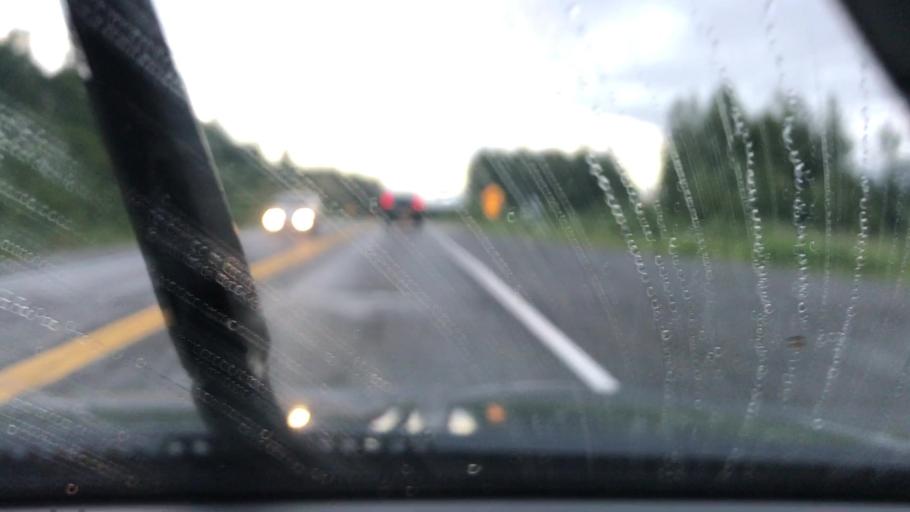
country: US
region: Alaska
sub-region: Matanuska-Susitna Borough
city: Y
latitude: 63.0423
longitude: -149.5830
